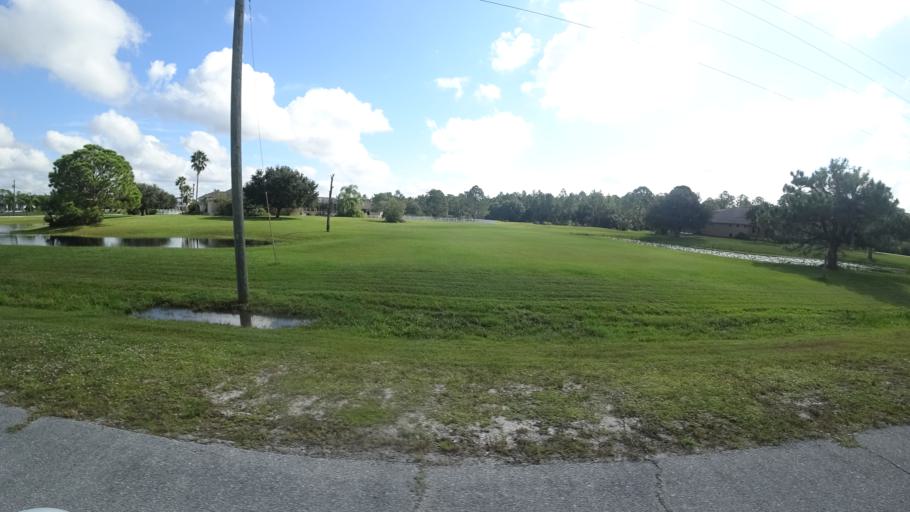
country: US
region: Florida
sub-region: Sarasota County
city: The Meadows
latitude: 27.4016
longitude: -82.3402
